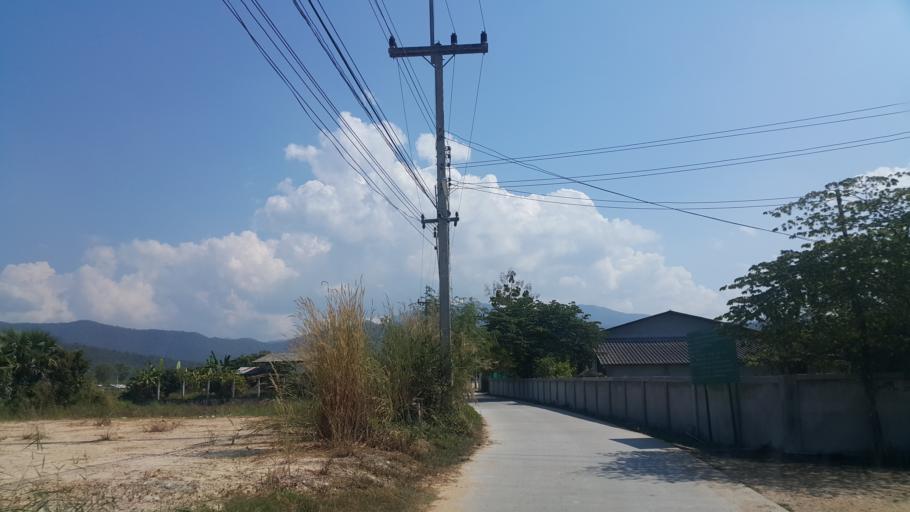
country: TH
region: Lamphun
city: Ban Thi
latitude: 18.6848
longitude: 99.1561
